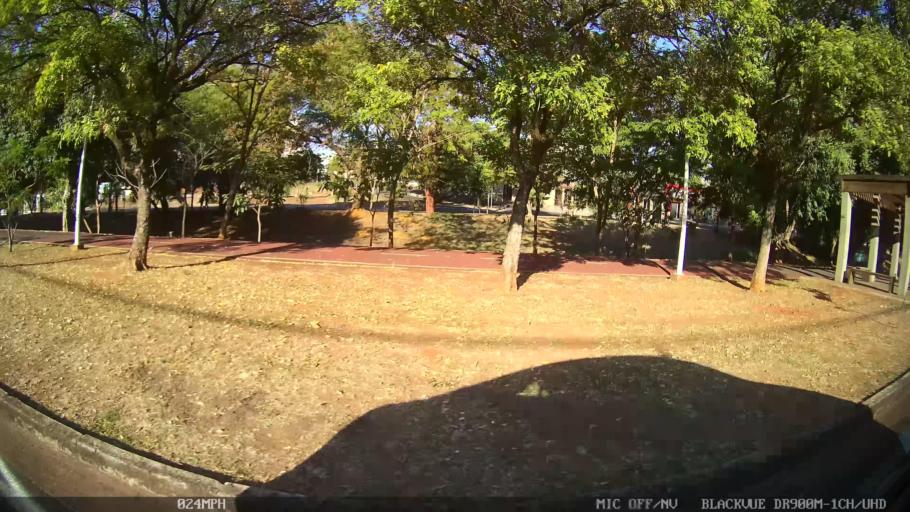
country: BR
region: Sao Paulo
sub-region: Sao Jose Do Rio Preto
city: Sao Jose do Rio Preto
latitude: -20.8286
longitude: -49.4047
